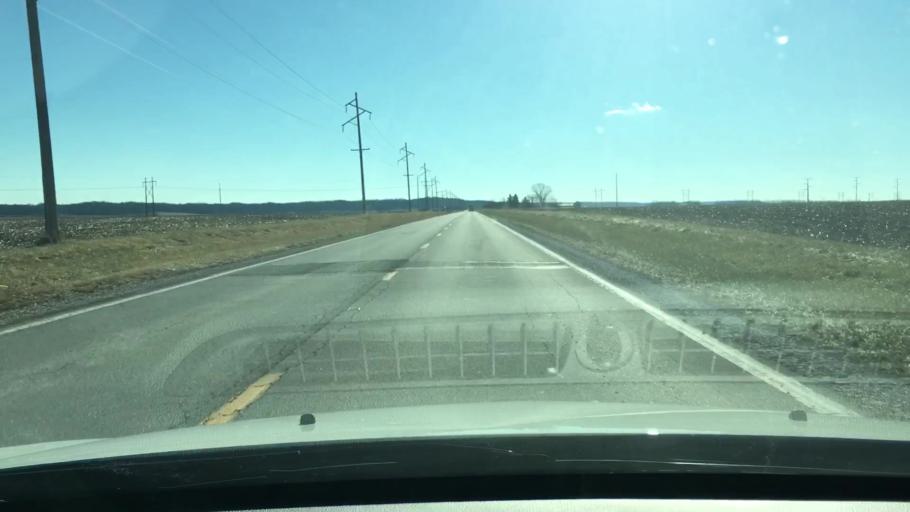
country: US
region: Illinois
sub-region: Morgan County
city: Meredosia
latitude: 39.8718
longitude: -90.5054
